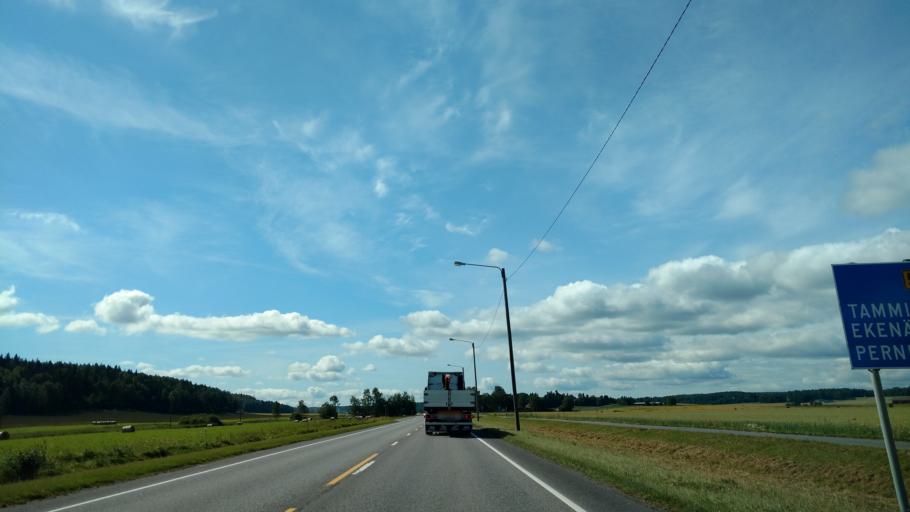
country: FI
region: Varsinais-Suomi
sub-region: Salo
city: Pernioe
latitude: 60.2482
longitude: 23.1323
